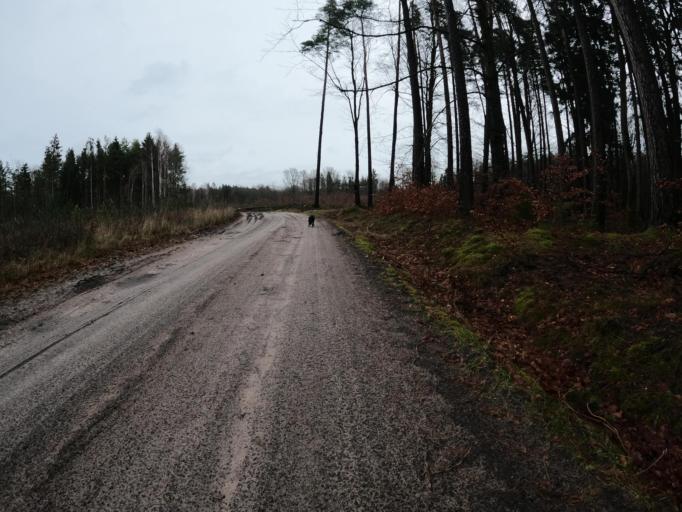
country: PL
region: West Pomeranian Voivodeship
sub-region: Powiat slawienski
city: Darlowo
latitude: 54.3915
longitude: 16.4798
